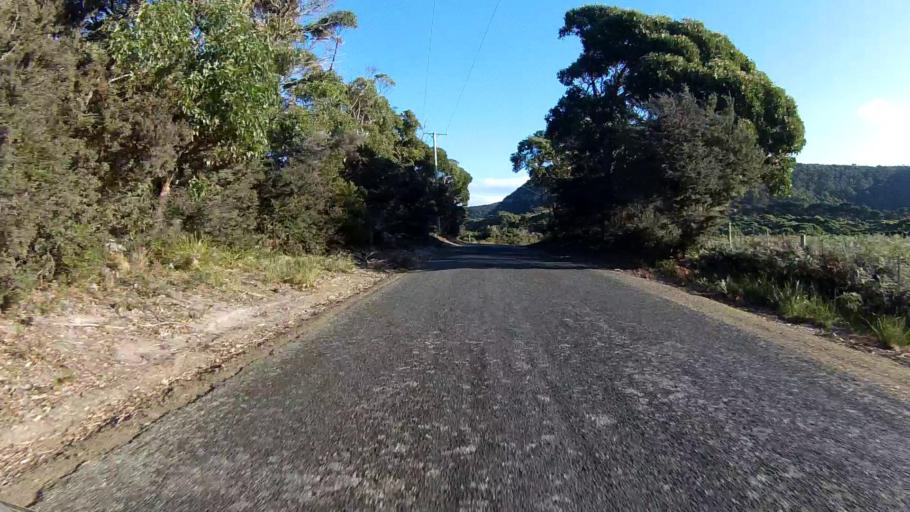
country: AU
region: Tasmania
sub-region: Clarence
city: Sandford
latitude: -43.1837
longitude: 147.8516
